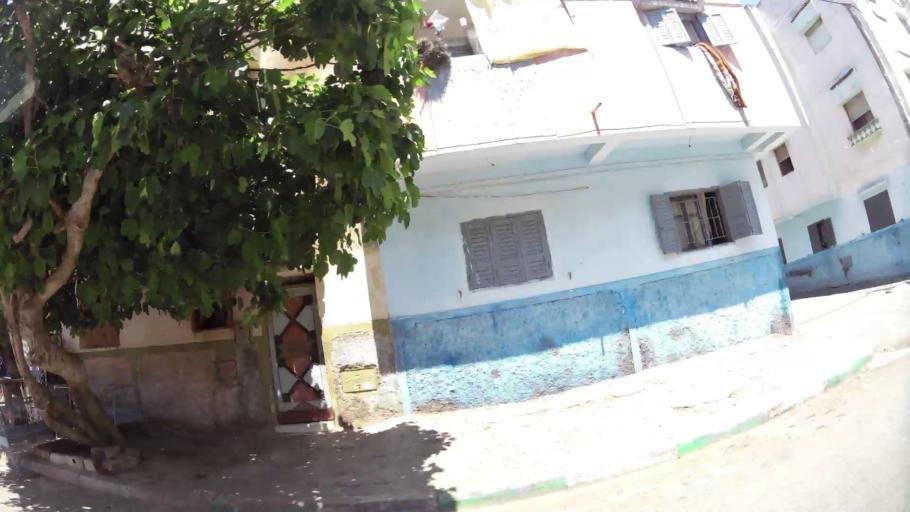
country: MA
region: Rabat-Sale-Zemmour-Zaer
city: Sale
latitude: 34.0660
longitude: -6.7863
